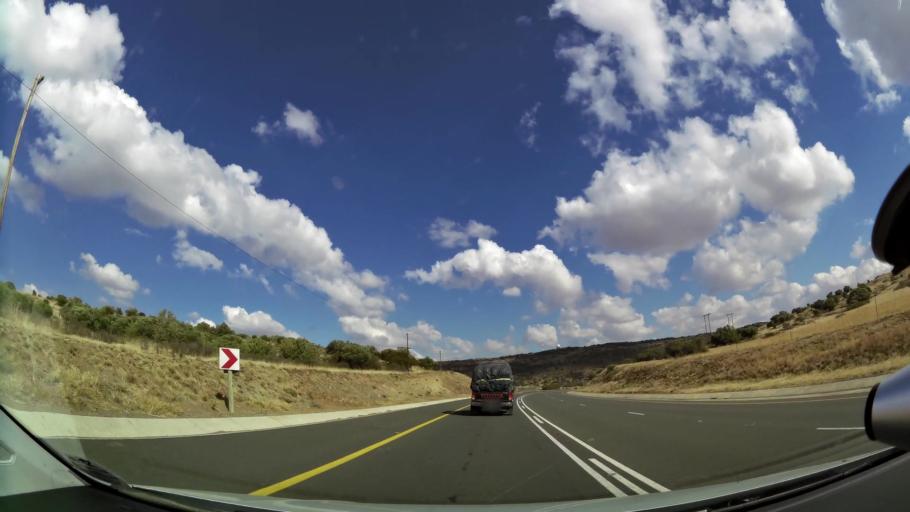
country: ZA
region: Orange Free State
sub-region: Mangaung Metropolitan Municipality
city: Bloemfontein
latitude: -29.1552
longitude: 26.0582
